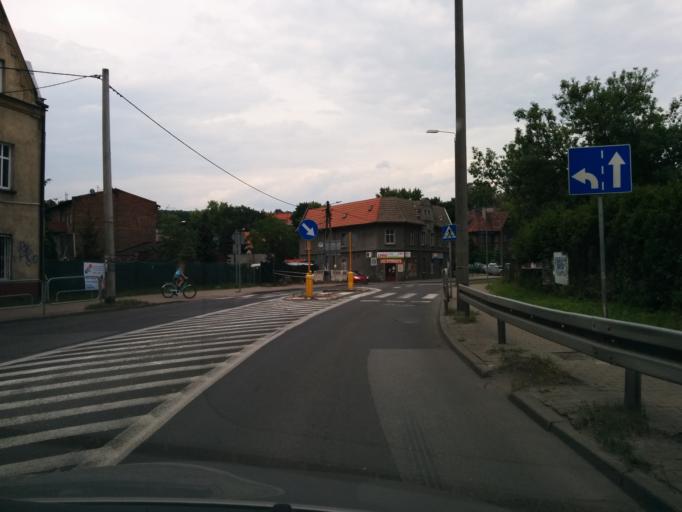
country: PL
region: Silesian Voivodeship
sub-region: Ruda Slaska
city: Ruda Slaska
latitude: 50.2689
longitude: 18.8381
